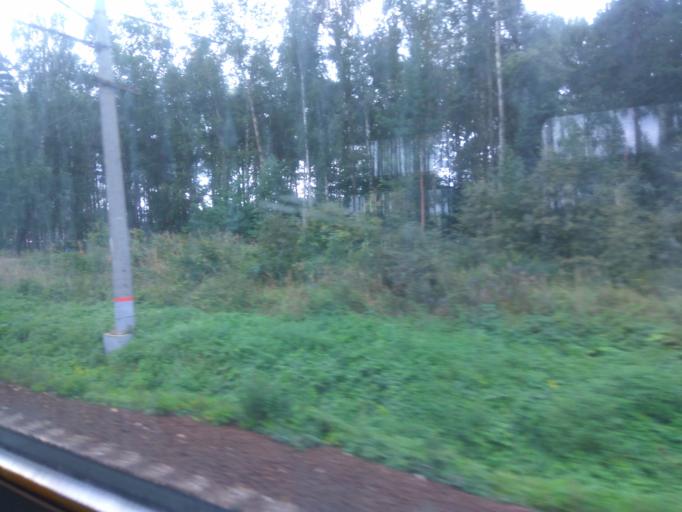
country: RU
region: Moskovskaya
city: Beloozerskiy
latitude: 55.4632
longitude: 38.4468
